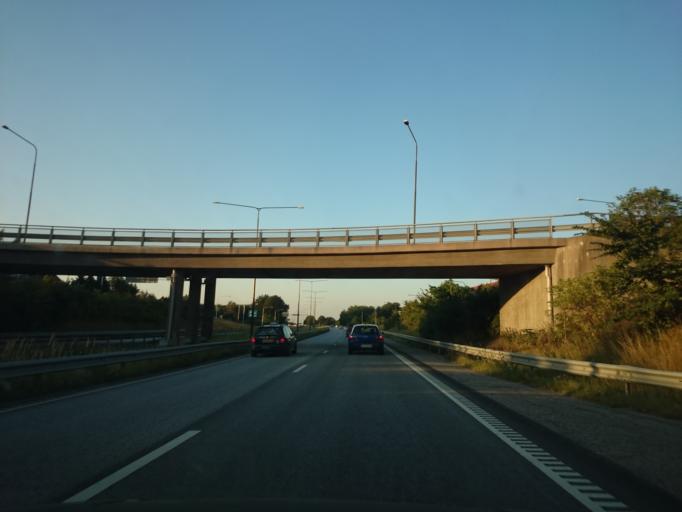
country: SE
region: Skane
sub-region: Malmo
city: Malmoe
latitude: 55.5699
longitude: 13.0456
